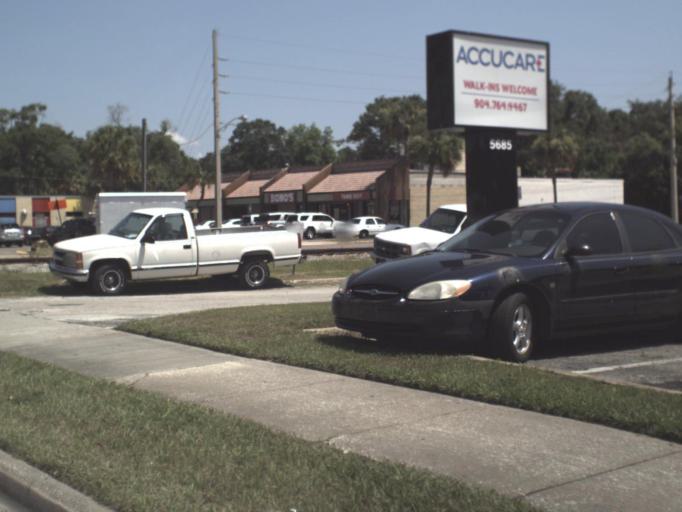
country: US
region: Florida
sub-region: Duval County
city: Jacksonville
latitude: 30.3742
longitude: -81.6659
